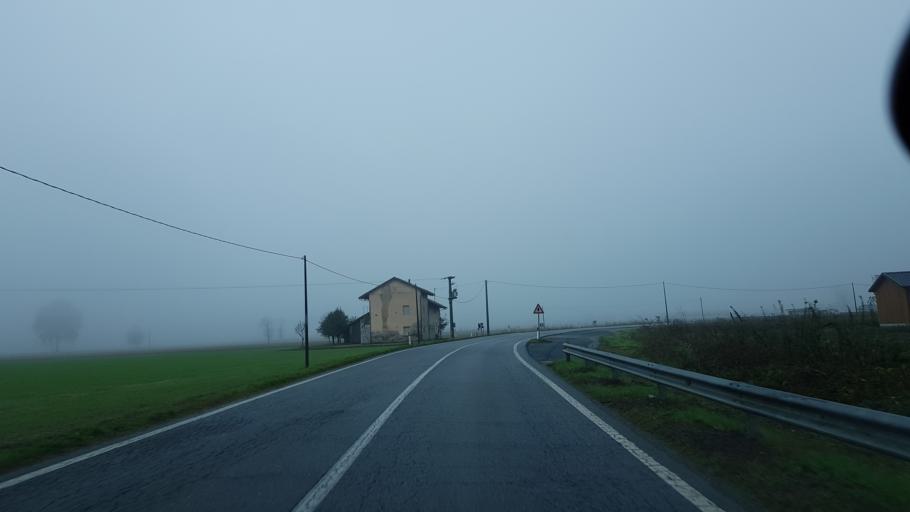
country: IT
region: Piedmont
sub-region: Provincia di Cuneo
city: Genola
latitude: 44.5568
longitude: 7.6378
